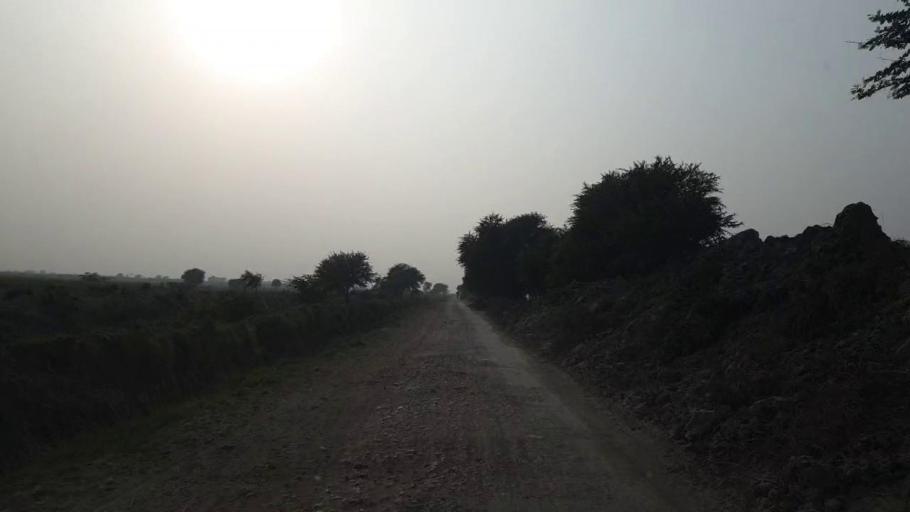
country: PK
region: Sindh
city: Mirpur Batoro
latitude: 24.6545
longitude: 68.3862
